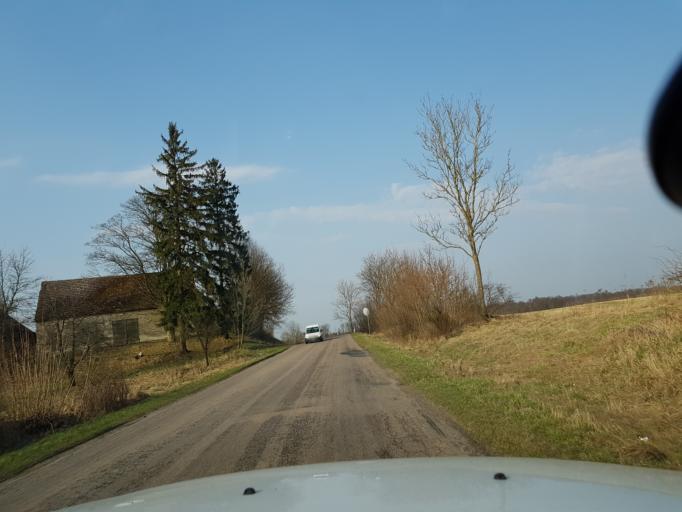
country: PL
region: West Pomeranian Voivodeship
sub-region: Powiat swidwinski
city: Polczyn-Zdroj
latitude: 53.7148
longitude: 16.0673
